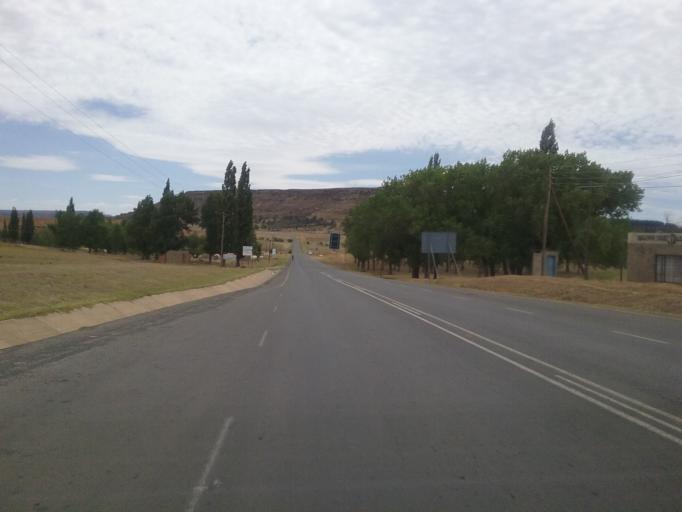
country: LS
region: Maseru
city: Nako
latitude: -29.6214
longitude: 27.4967
